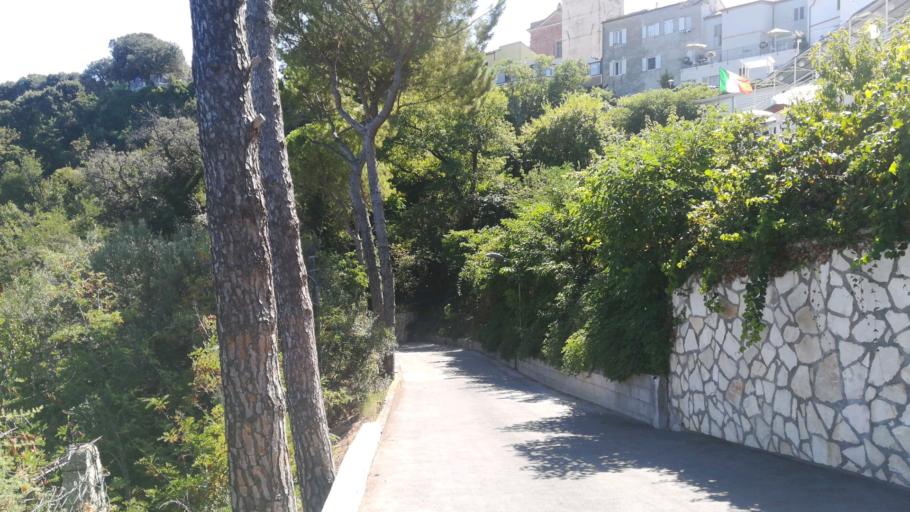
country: IT
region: The Marches
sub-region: Provincia di Ancona
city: Sirolo
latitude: 43.5240
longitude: 13.6200
